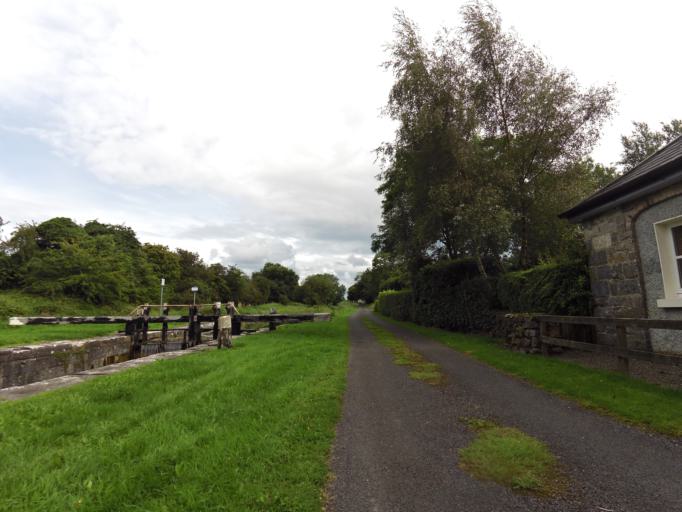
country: IE
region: Leinster
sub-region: An Iarmhi
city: An Muileann gCearr
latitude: 53.5592
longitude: -7.4885
